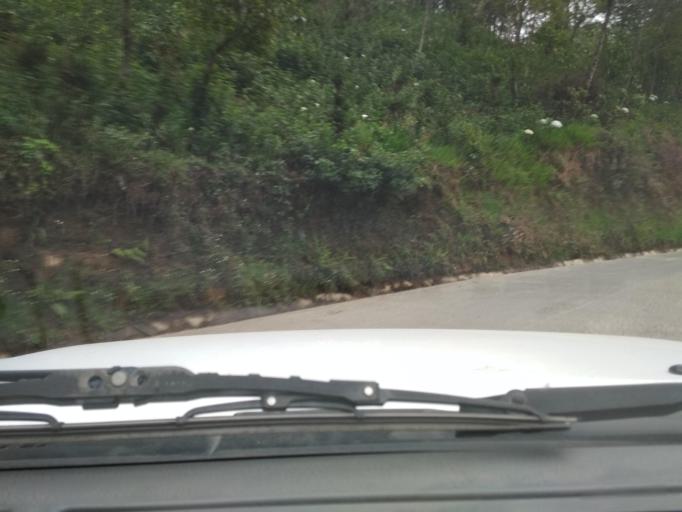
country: MX
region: Veracruz
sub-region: La Perla
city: Chilapa
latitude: 18.9725
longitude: -97.1658
